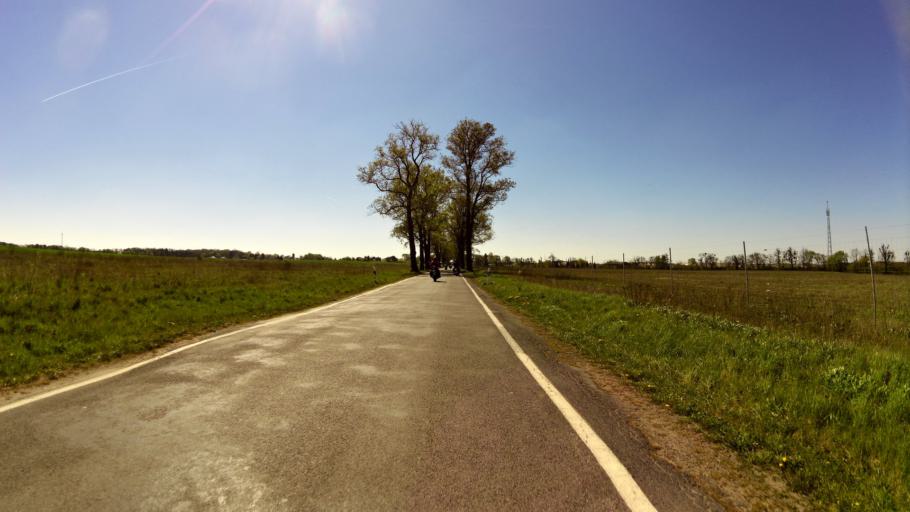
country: DE
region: Brandenburg
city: Werftpfuhl
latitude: 52.6480
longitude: 13.7923
